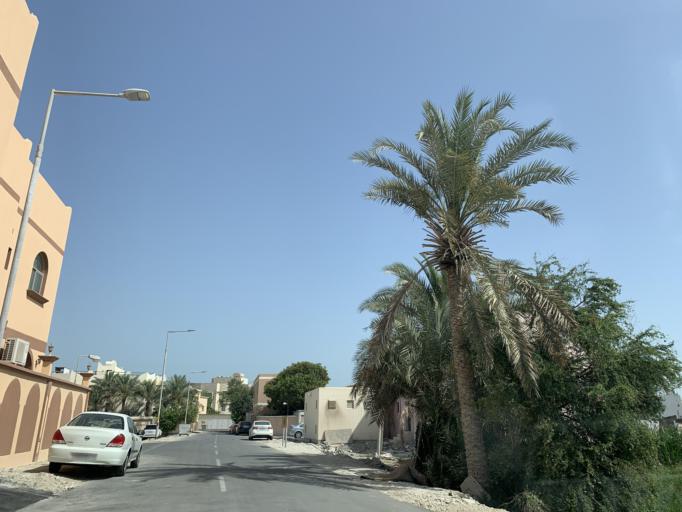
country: BH
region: Northern
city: Sitrah
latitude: 26.1441
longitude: 50.6053
